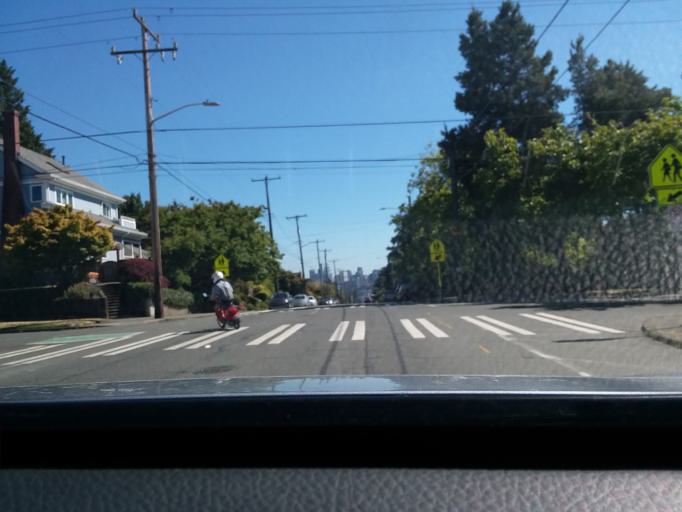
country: US
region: Washington
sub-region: King County
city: Seattle
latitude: 47.6593
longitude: -122.3363
